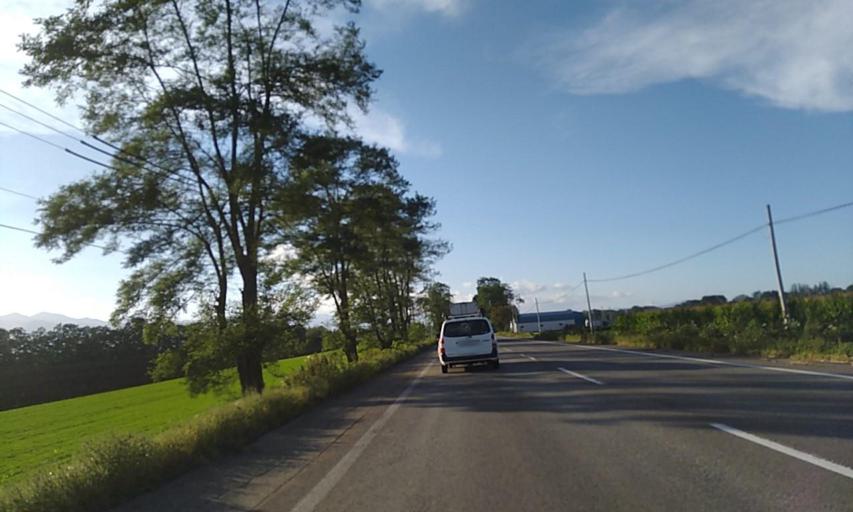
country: JP
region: Hokkaido
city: Obihiro
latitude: 42.9247
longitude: 142.9889
